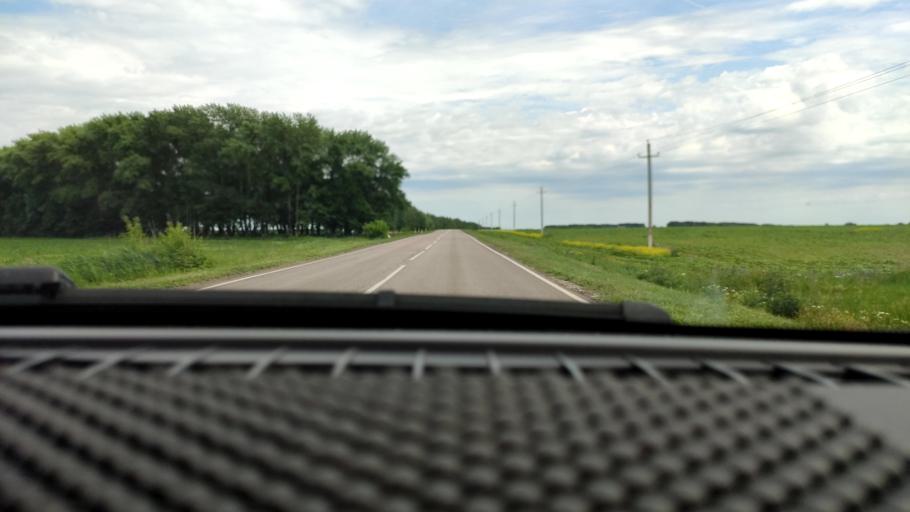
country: RU
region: Voronezj
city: Panino
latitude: 51.6564
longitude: 39.9997
